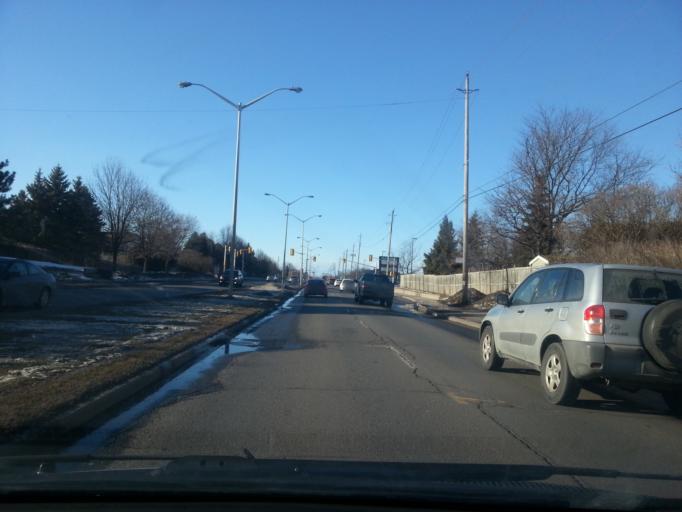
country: CA
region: Quebec
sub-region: Outaouais
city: Gatineau
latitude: 45.4646
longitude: -75.4900
